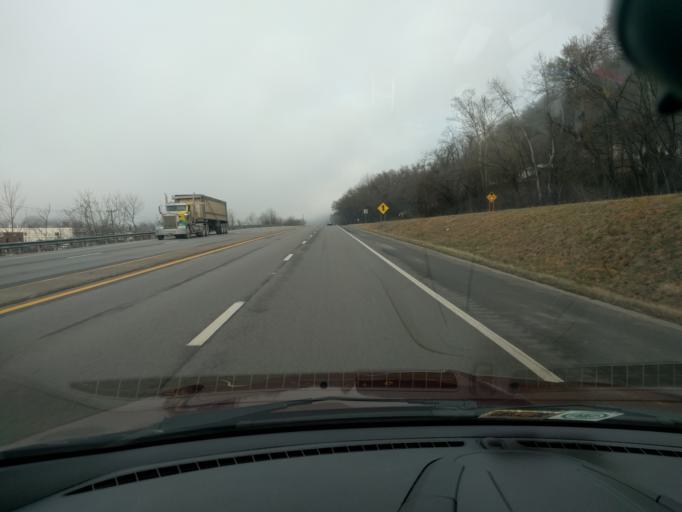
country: US
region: West Virginia
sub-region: Kanawha County
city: Chesapeake
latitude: 38.2265
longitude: -81.5304
